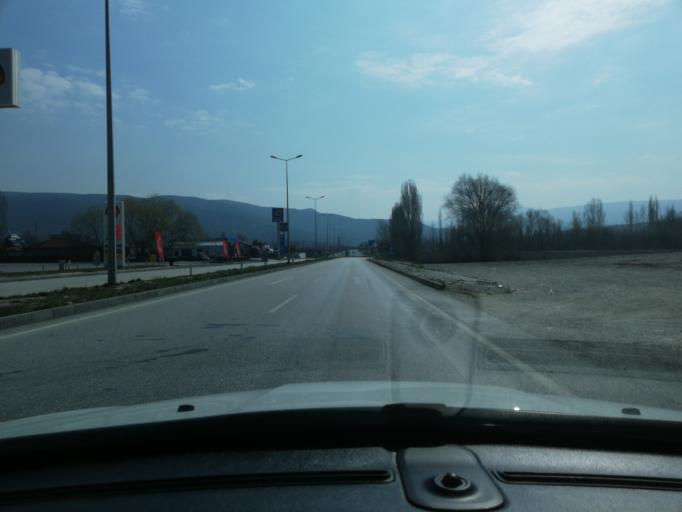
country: TR
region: Cankiri
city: Ilgaz
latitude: 40.9061
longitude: 33.6458
